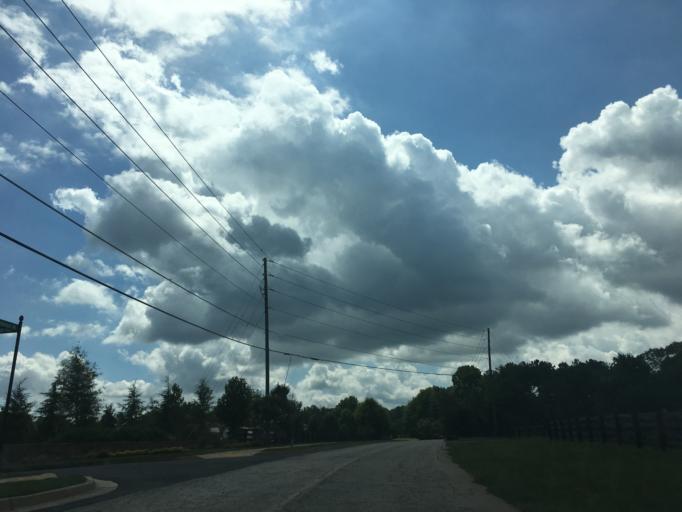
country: US
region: Georgia
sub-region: Fulton County
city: Roswell
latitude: 34.0969
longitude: -84.3773
